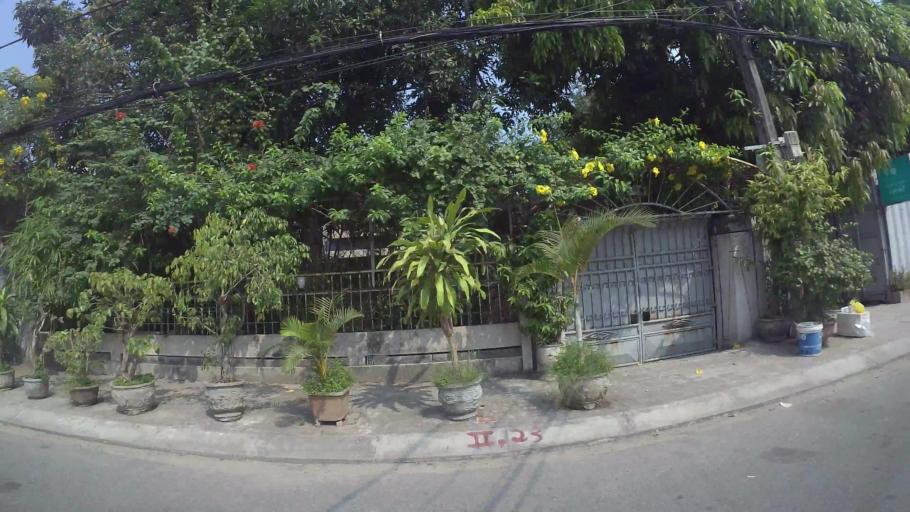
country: VN
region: Da Nang
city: Son Tra
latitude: 16.0434
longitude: 108.2440
